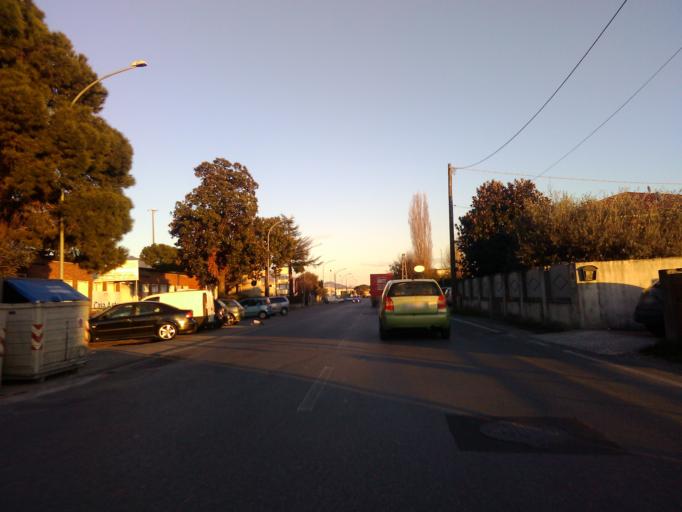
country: IT
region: Tuscany
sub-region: Provincia di Massa-Carrara
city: Carrara
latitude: 44.0358
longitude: 10.0803
